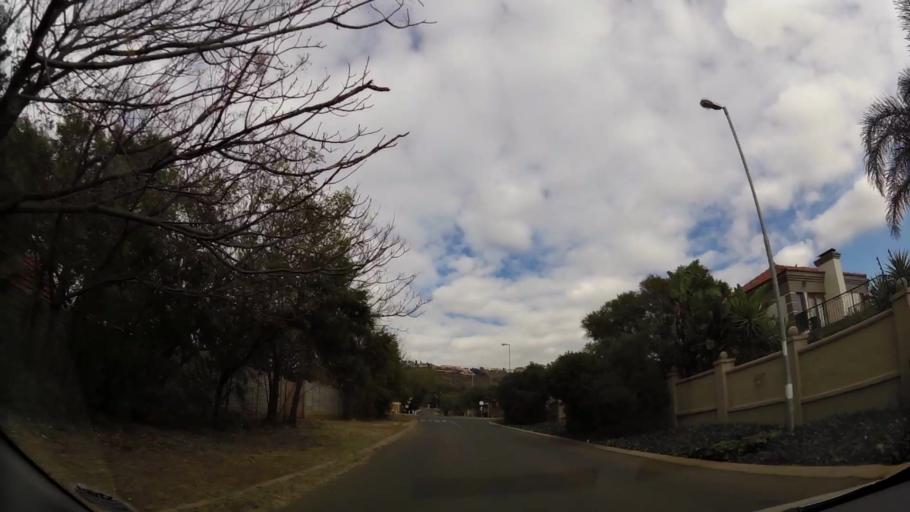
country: ZA
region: Gauteng
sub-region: City of Johannesburg Metropolitan Municipality
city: Roodepoort
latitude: -26.0975
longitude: 27.8714
